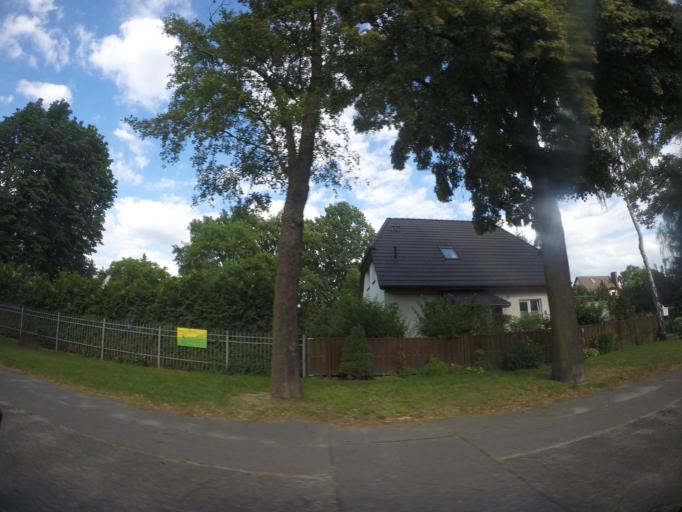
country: DE
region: Berlin
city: Karlshorst
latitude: 52.4772
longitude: 13.5595
